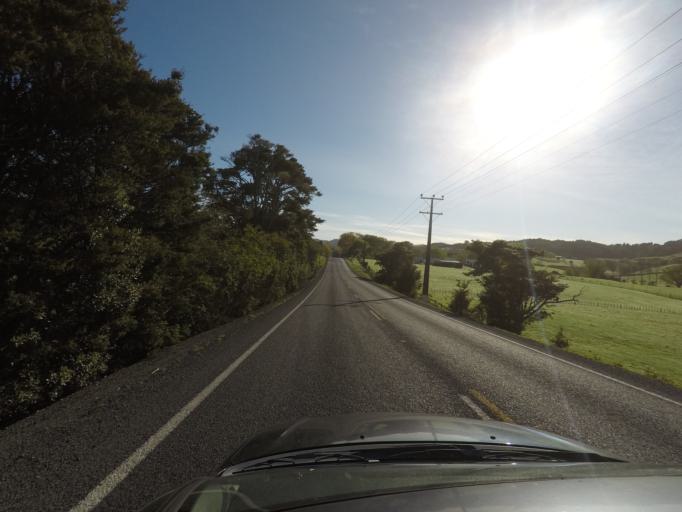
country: NZ
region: Auckland
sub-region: Auckland
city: Red Hill
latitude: -36.9909
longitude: 174.9879
